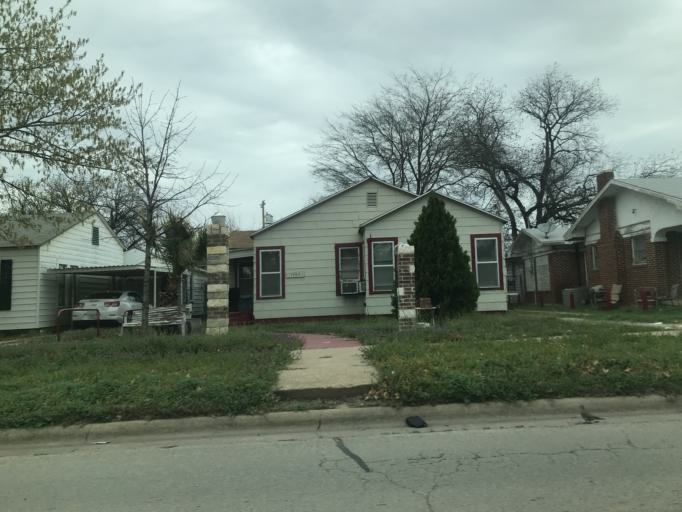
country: US
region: Texas
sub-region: Taylor County
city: Abilene
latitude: 32.4608
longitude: -99.7418
